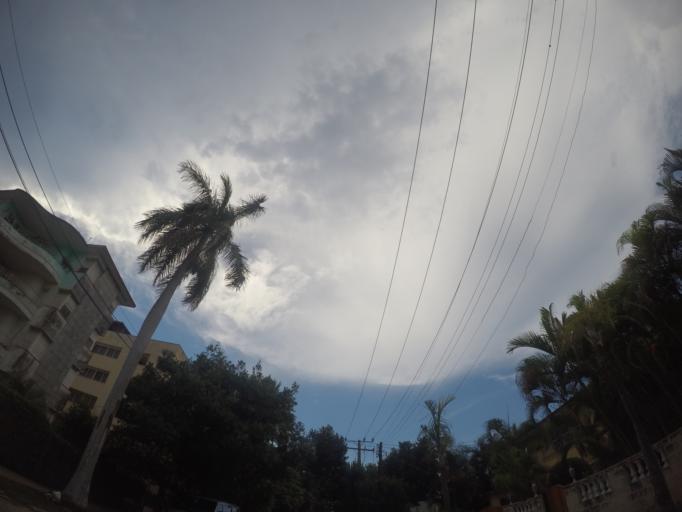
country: CU
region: La Habana
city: Havana
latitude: 23.1209
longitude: -82.4246
